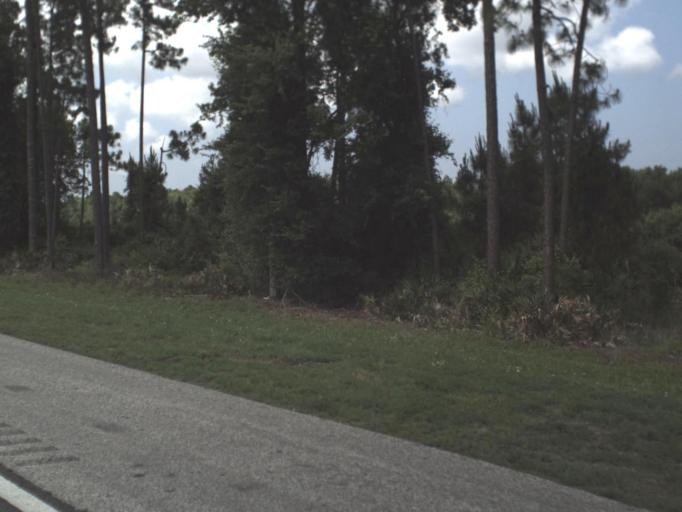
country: US
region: Florida
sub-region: Saint Johns County
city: Saint Augustine Shores
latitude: 29.7144
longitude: -81.3329
